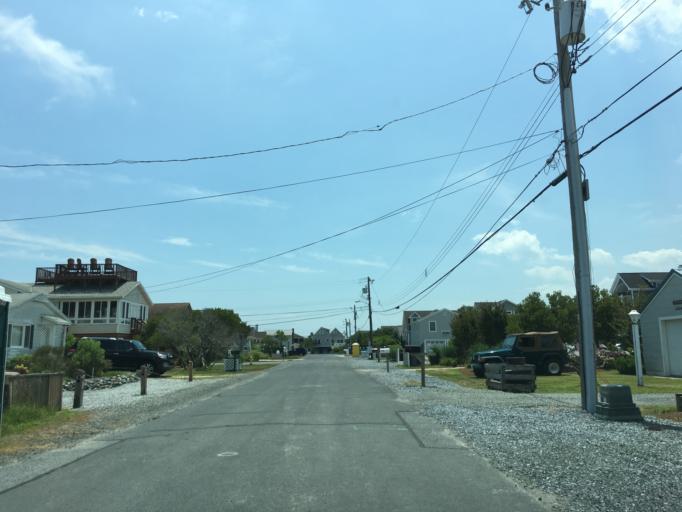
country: US
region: Delaware
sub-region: Sussex County
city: Bethany Beach
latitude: 38.4640
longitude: -75.0542
